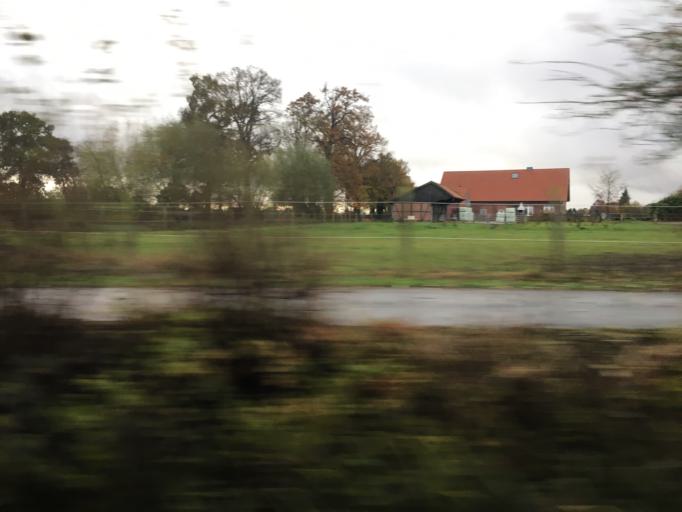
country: DE
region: North Rhine-Westphalia
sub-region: Regierungsbezirk Munster
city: Altenberge
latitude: 52.0340
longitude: 7.5187
